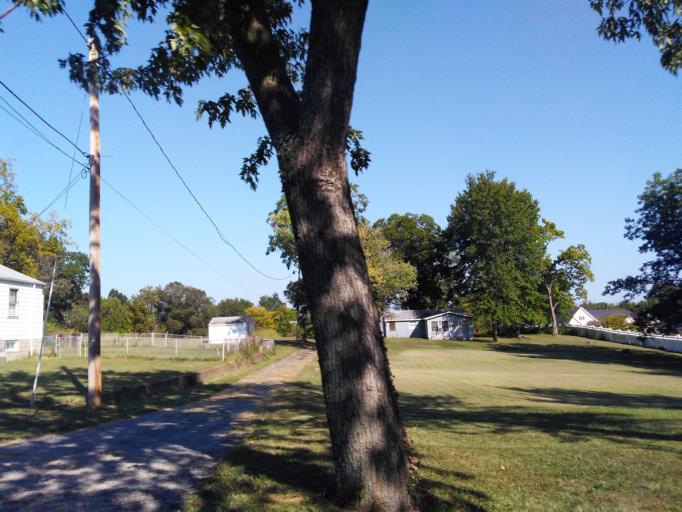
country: US
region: Missouri
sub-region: Saint Louis County
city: Green Park
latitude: 38.5125
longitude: -90.3430
